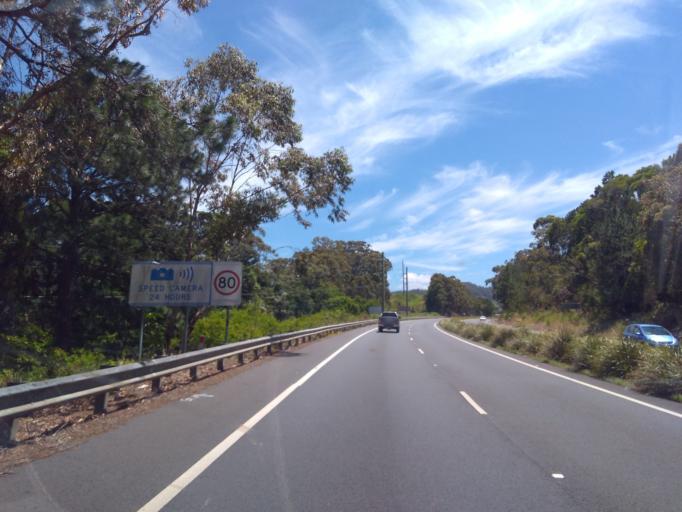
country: AU
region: New South Wales
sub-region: Coffs Harbour
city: Coffs Harbour
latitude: -30.2633
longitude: 153.1289
